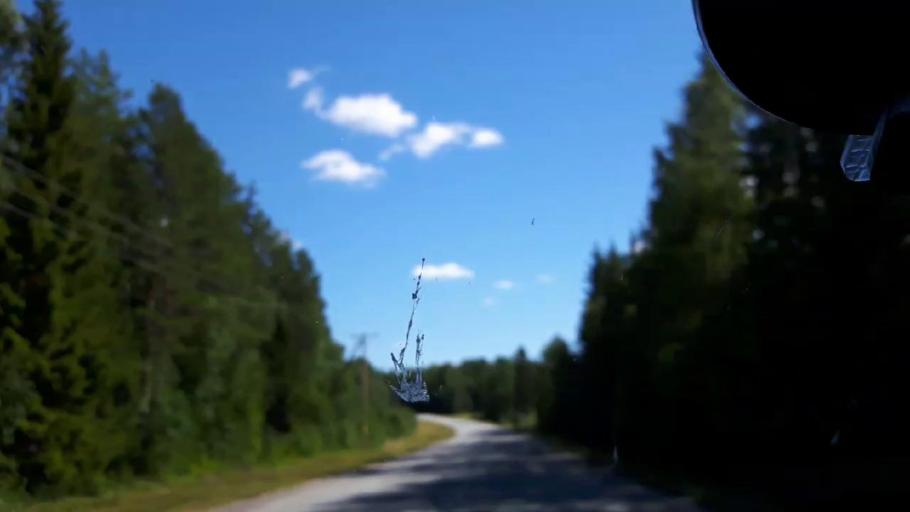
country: SE
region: Vaesternorrland
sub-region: Ange Kommun
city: Fransta
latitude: 62.7052
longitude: 16.3623
